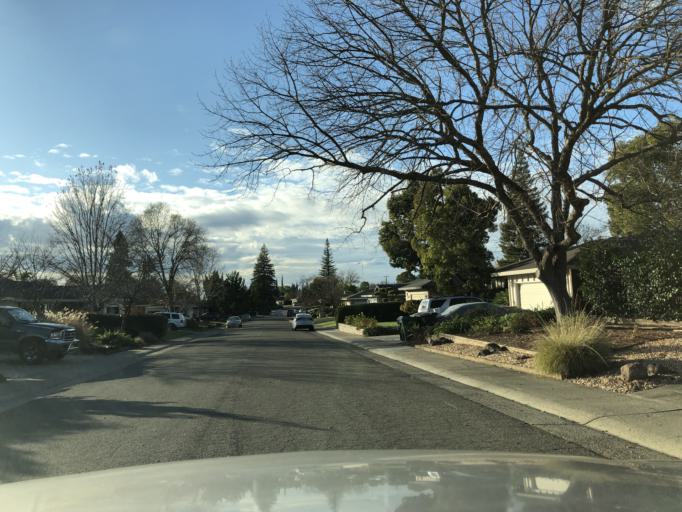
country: US
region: California
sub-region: Sacramento County
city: Foothill Farms
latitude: 38.6575
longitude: -121.3156
